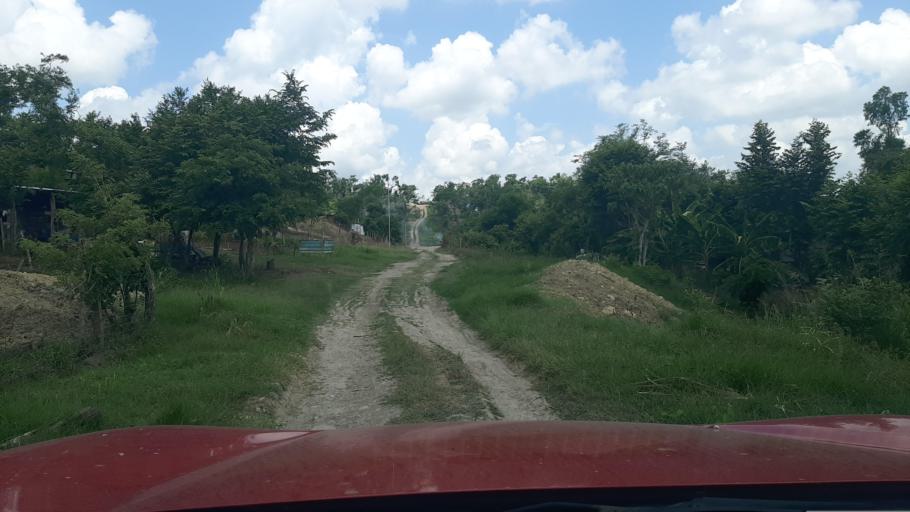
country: MX
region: Veracruz
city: Coatzintla
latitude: 20.5034
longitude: -97.4580
